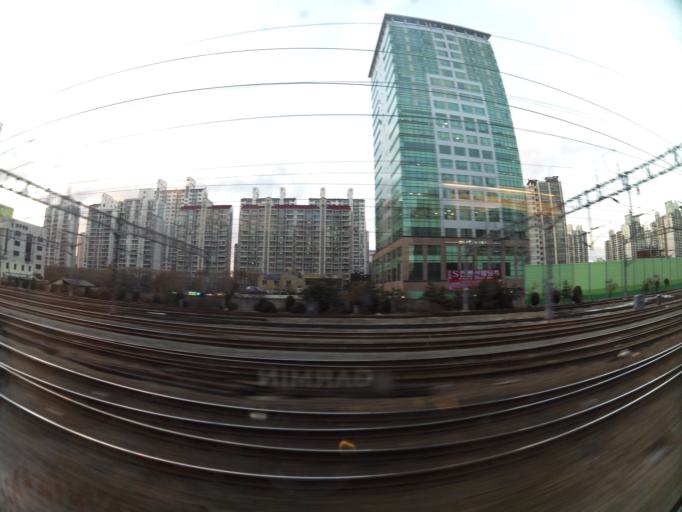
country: KR
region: Gyeonggi-do
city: Kwangmyong
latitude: 37.5046
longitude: 126.8841
